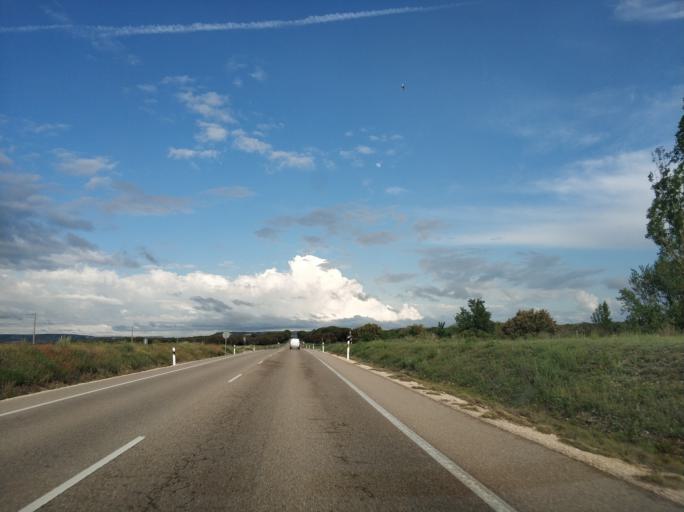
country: ES
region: Castille and Leon
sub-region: Provincia de Valladolid
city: Quintanilla de Arriba
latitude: 41.6151
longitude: -4.1893
